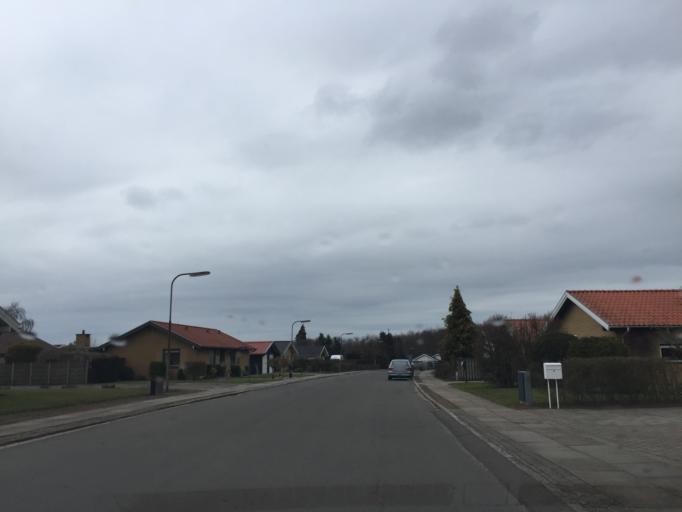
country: DK
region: South Denmark
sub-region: Odense Kommune
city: Odense
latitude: 55.4176
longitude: 10.3395
